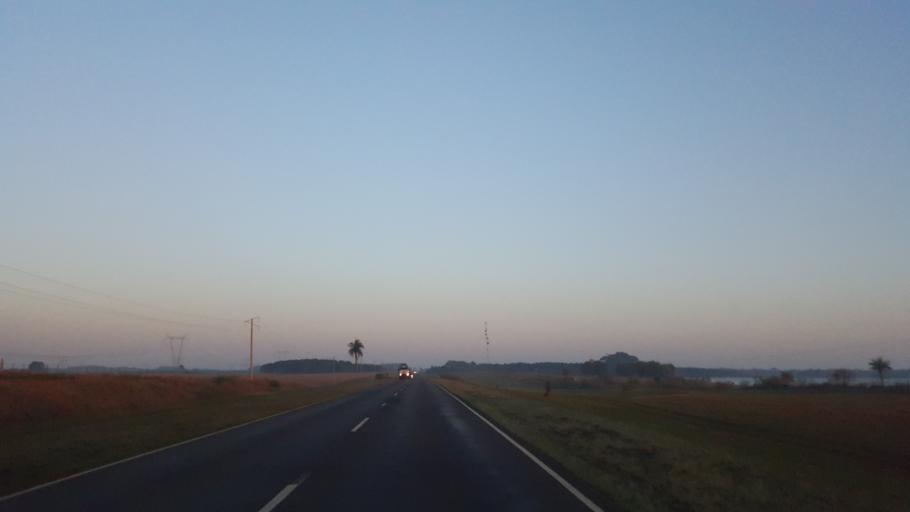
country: AR
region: Corrientes
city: Ituzaingo
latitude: -27.5889
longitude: -56.4829
